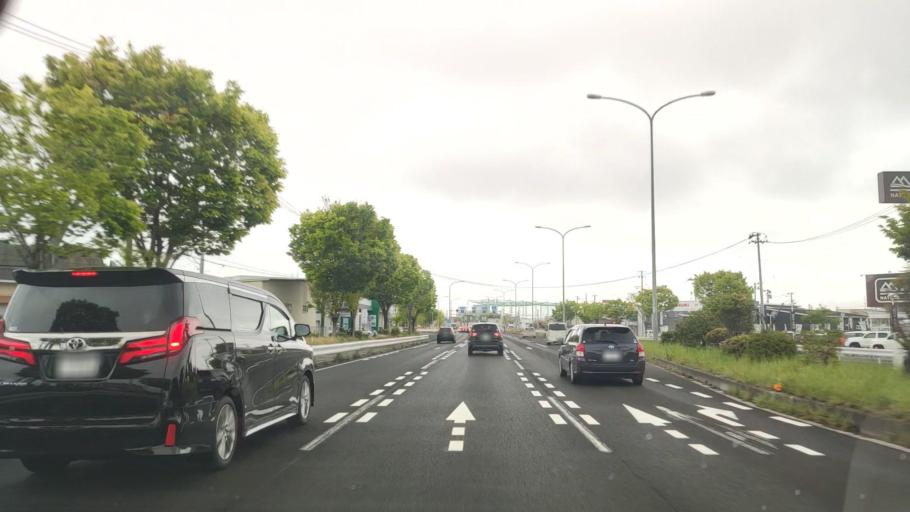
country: JP
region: Miyagi
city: Sendai-shi
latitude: 38.2419
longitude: 140.9202
